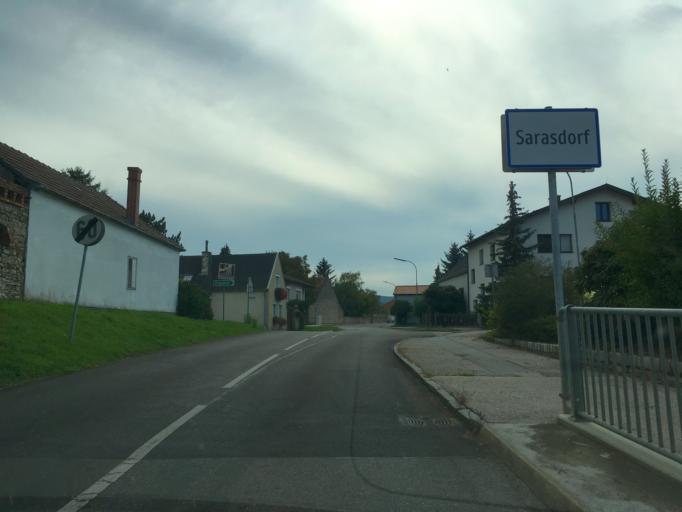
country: AT
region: Lower Austria
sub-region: Politischer Bezirk Bruck an der Leitha
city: Trautmannsdorf an der Leitha
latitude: 48.0225
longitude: 16.6778
